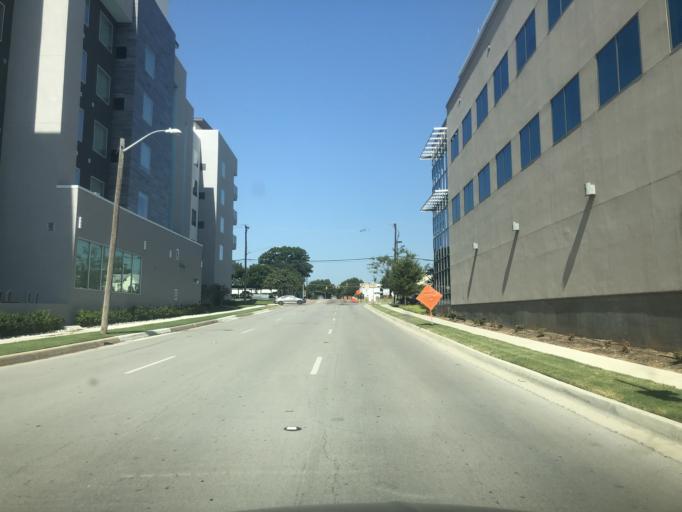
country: US
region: Texas
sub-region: Tarrant County
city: Fort Worth
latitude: 32.7309
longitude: -97.3678
